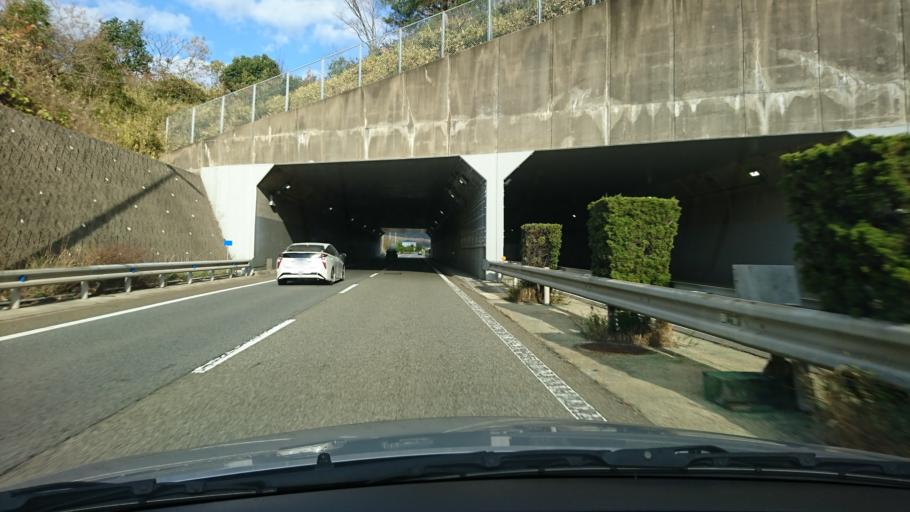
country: JP
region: Hyogo
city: Kobe
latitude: 34.7532
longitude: 135.1414
